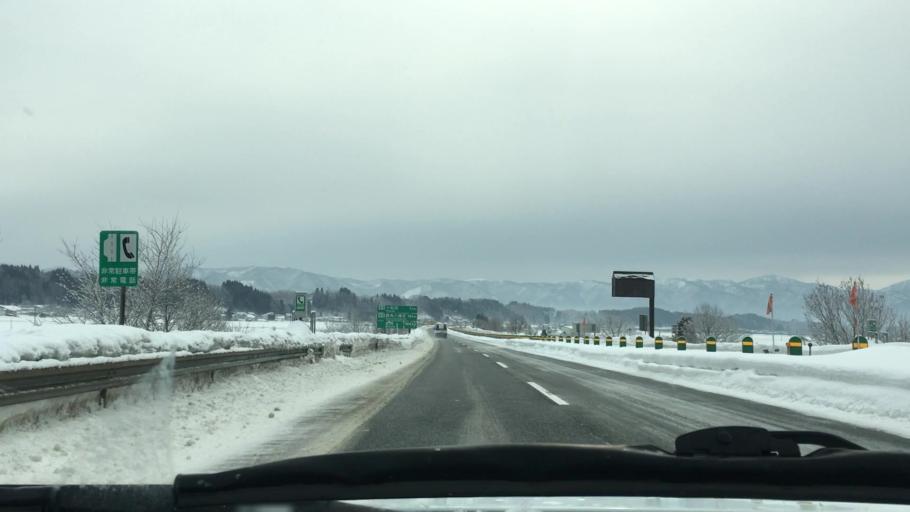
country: JP
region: Akita
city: Hanawa
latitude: 40.3011
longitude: 140.7457
